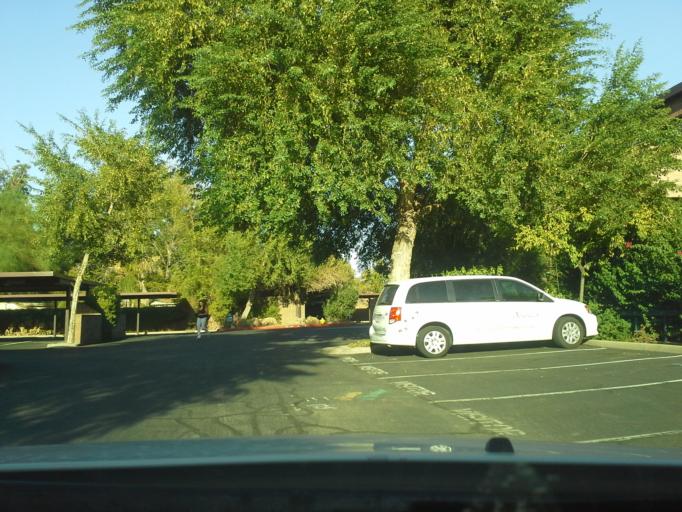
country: US
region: Arizona
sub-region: Maricopa County
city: Phoenix
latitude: 33.4703
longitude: -112.0683
